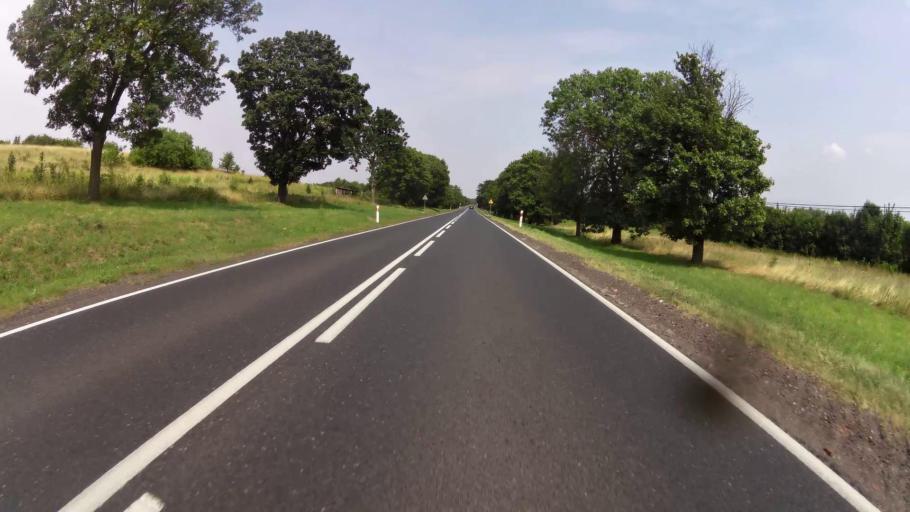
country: PL
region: West Pomeranian Voivodeship
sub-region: Powiat mysliborski
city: Mysliborz
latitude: 52.9303
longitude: 14.8886
